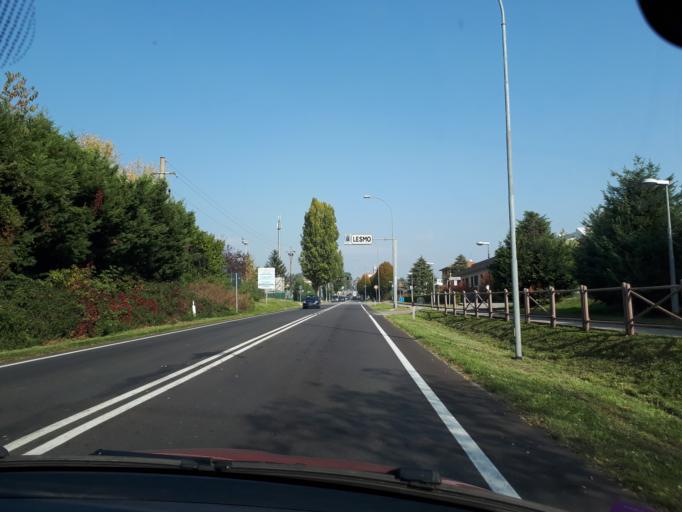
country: IT
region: Lombardy
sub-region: Provincia di Monza e Brianza
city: Lesmo
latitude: 45.6415
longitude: 9.3047
